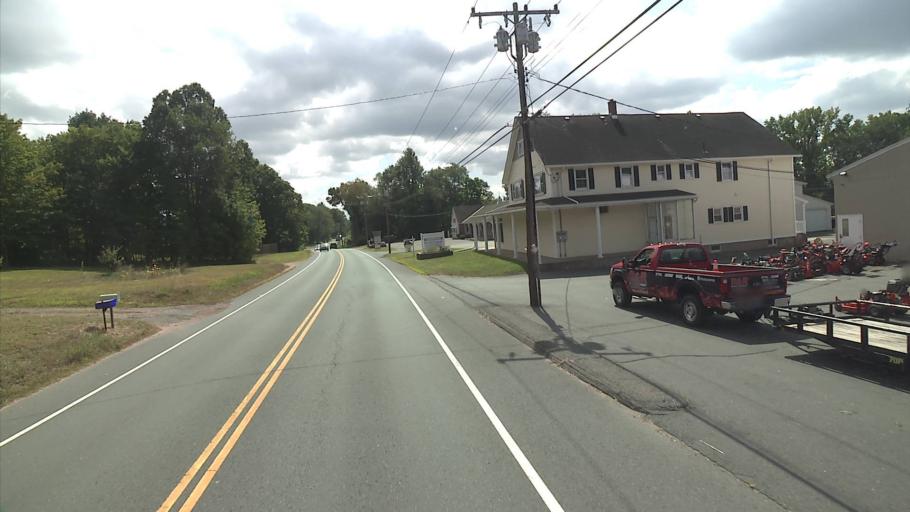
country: US
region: Connecticut
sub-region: Hartford County
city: Salmon Brook
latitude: 41.9392
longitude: -72.7741
